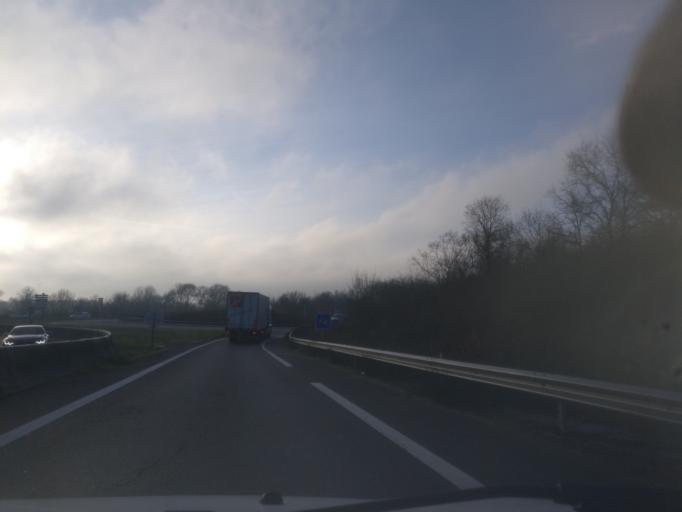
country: FR
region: Pays de la Loire
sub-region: Departement de la Loire-Atlantique
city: Sainte-Luce-sur-Loire
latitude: 47.2365
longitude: -1.4830
